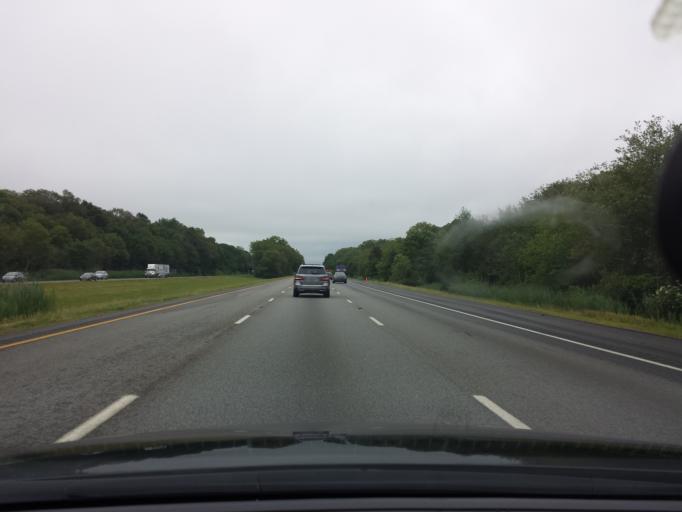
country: US
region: Massachusetts
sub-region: Bristol County
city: Ocean Grove
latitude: 41.7591
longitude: -71.2287
